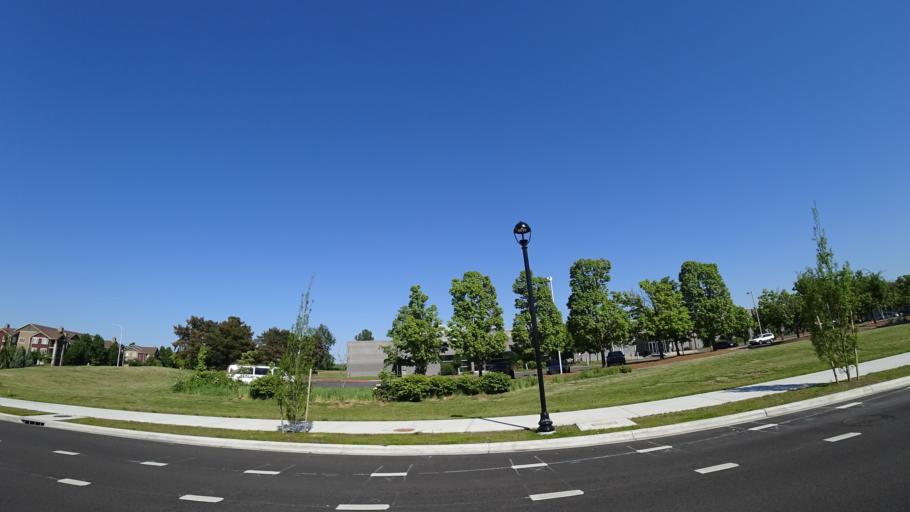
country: US
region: Oregon
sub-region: Washington County
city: Rockcreek
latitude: 45.5334
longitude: -122.9119
